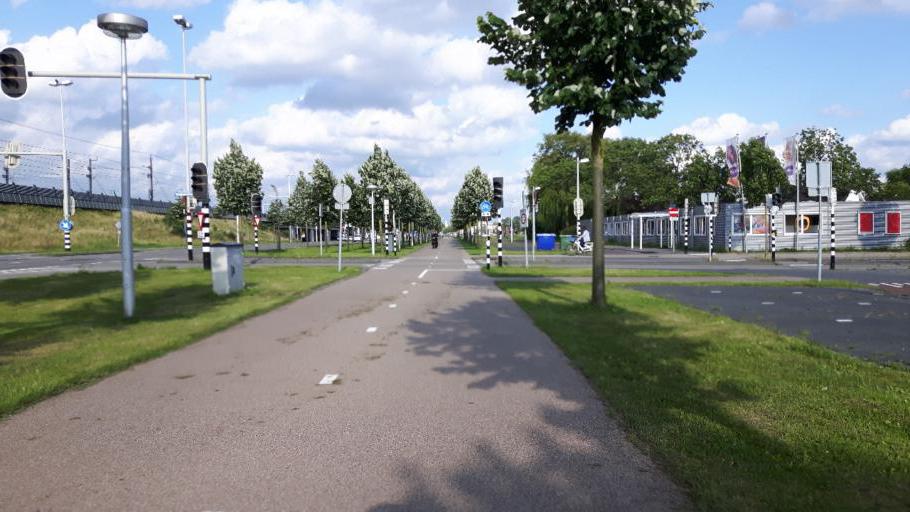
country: NL
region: Utrecht
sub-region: Stichtse Vecht
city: Maarssen
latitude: 52.1001
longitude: 5.0385
